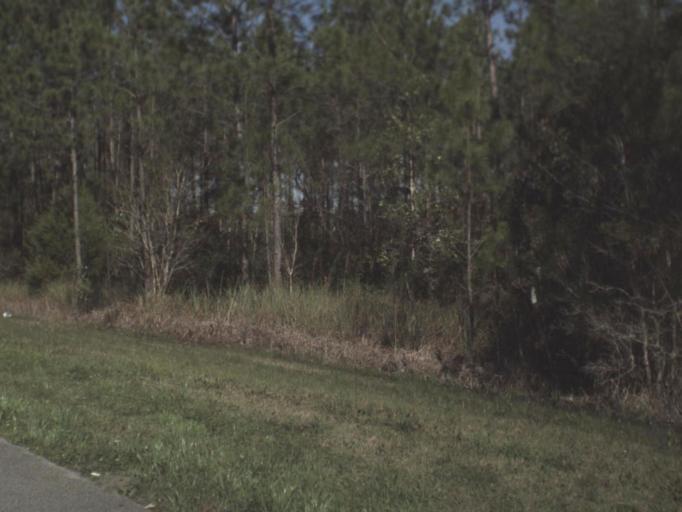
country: US
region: Florida
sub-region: Gulf County
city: Port Saint Joe
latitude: 29.9001
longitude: -85.2110
